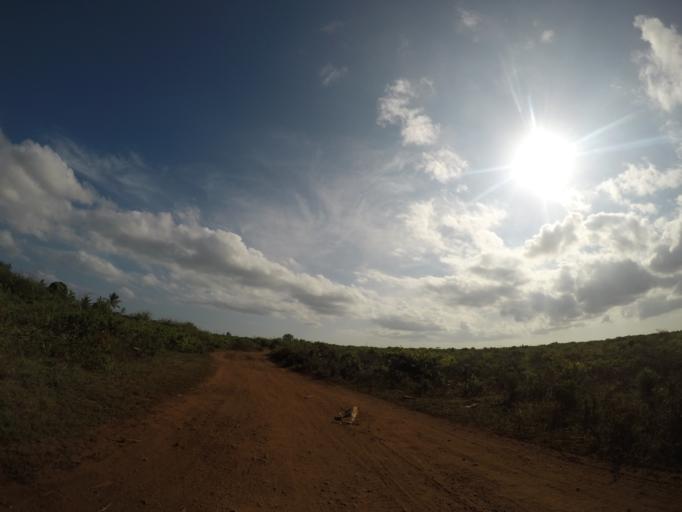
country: TZ
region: Zanzibar Central/South
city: Koani
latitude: -6.2066
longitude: 39.3144
